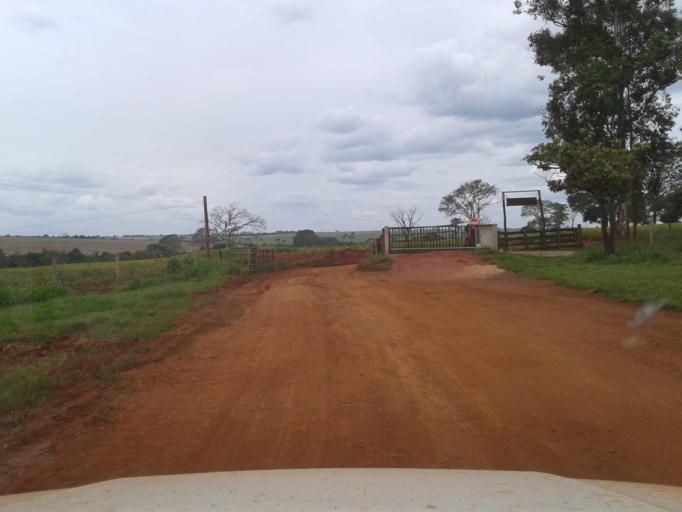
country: BR
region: Minas Gerais
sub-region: Centralina
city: Centralina
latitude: -18.7733
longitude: -49.2213
